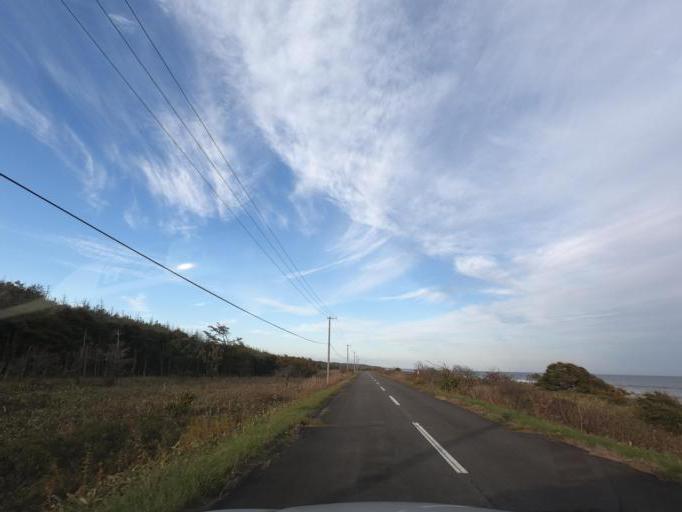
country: JP
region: Hokkaido
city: Obihiro
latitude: 42.5389
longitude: 143.4892
